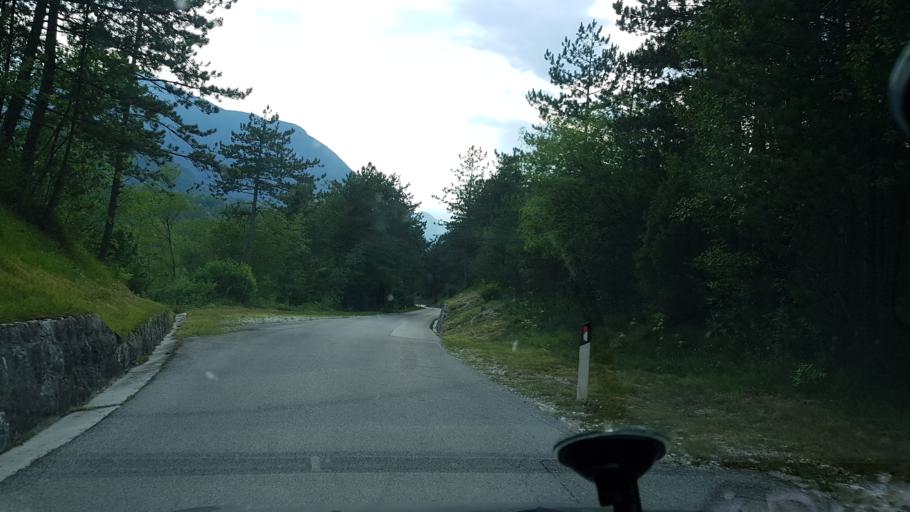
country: IT
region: Friuli Venezia Giulia
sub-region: Provincia di Udine
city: Prato
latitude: 46.3642
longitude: 13.3342
